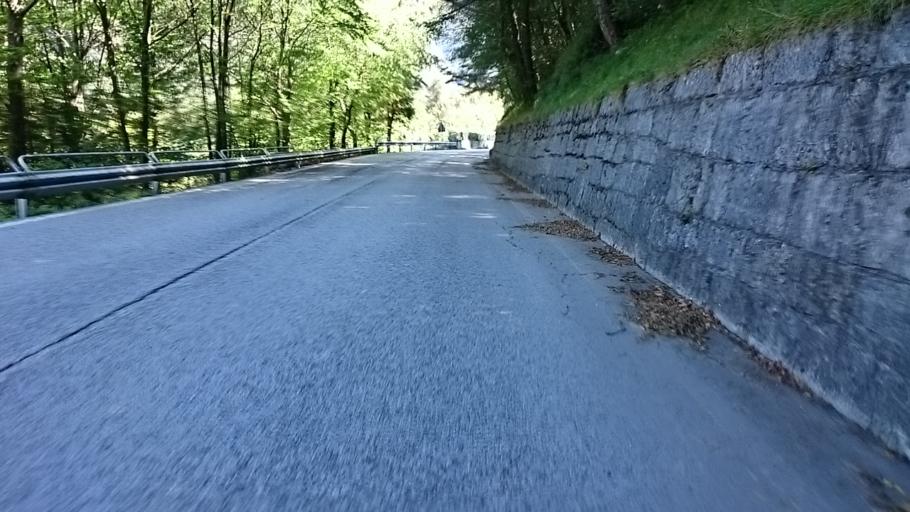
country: IT
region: Veneto
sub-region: Provincia di Belluno
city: Perarolo di Cadore
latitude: 46.3782
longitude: 12.3536
